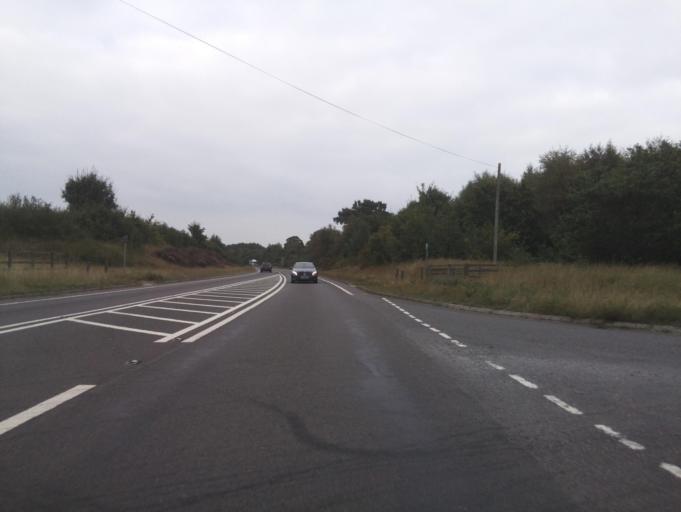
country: GB
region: England
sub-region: Shropshire
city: Stoke upon Tern
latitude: 52.8487
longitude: -2.5582
